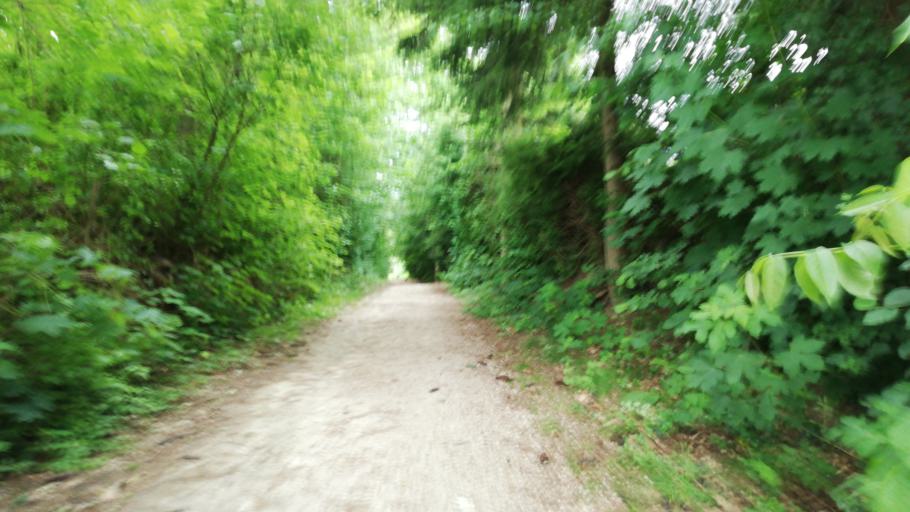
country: AT
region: Upper Austria
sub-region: Politischer Bezirk Grieskirchen
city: Bad Schallerbach
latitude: 48.2328
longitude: 13.9231
